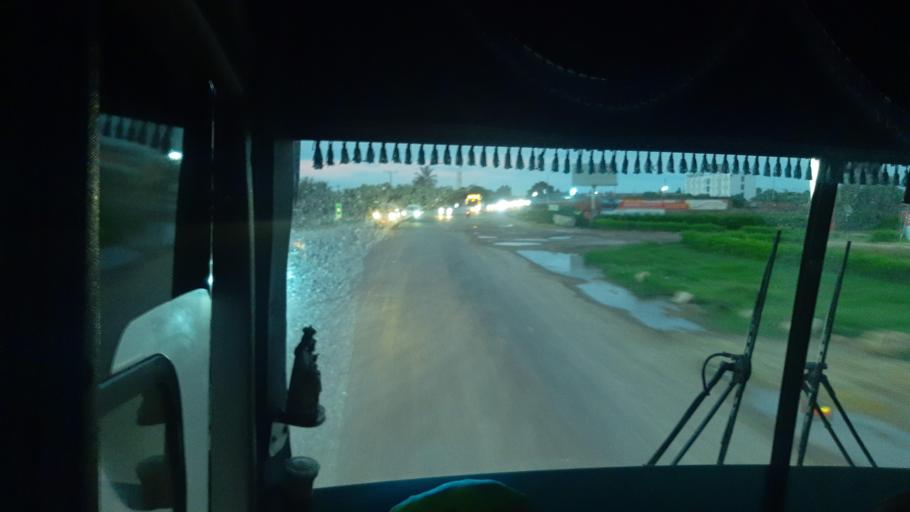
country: CO
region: Atlantico
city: Barranquilla
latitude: 10.9593
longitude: -74.7443
